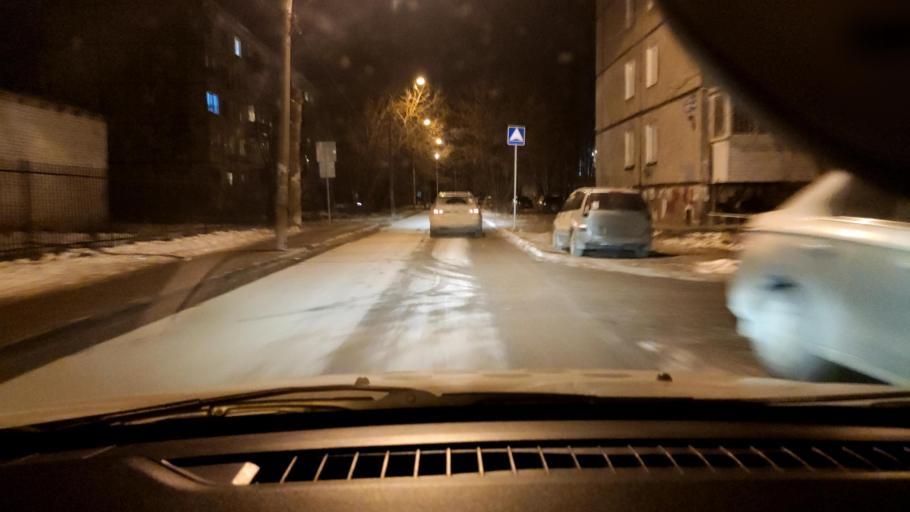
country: RU
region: Perm
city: Kultayevo
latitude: 58.0144
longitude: 55.9723
